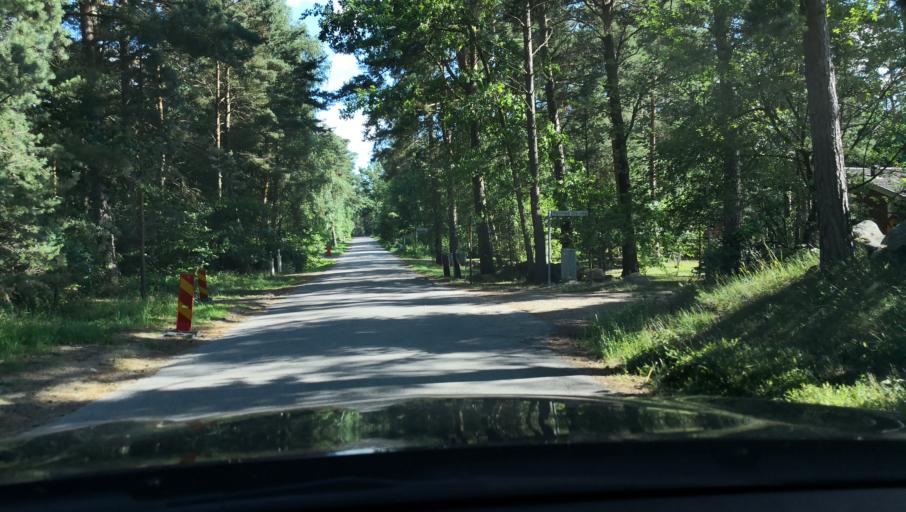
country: SE
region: Skane
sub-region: Simrishamns Kommun
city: Kivik
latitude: 55.7801
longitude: 14.1940
